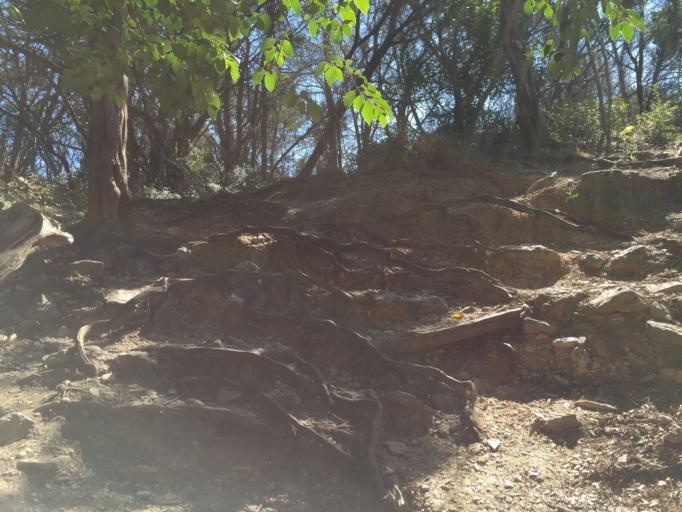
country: US
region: Texas
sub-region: Travis County
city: Rollingwood
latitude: 30.2635
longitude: -97.7729
